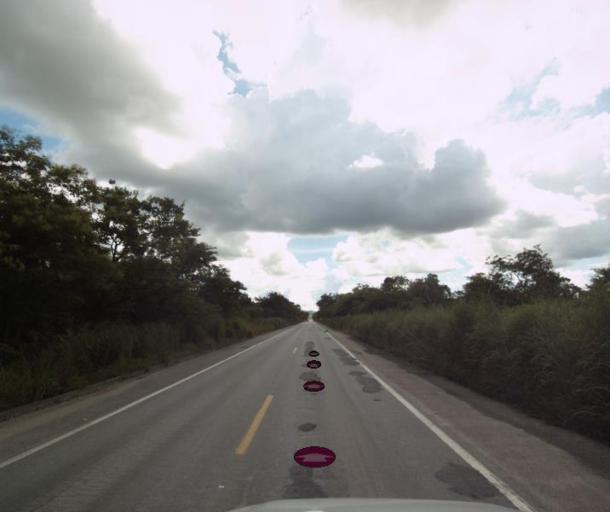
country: BR
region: Goias
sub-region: Porangatu
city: Porangatu
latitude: -13.5541
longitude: -49.0795
